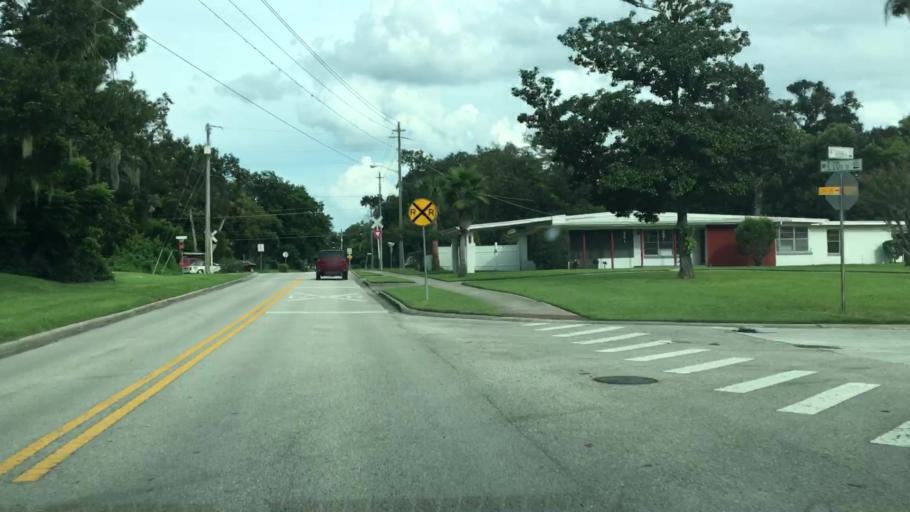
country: US
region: Florida
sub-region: Seminole County
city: Sanford
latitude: 28.7940
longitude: -81.2622
